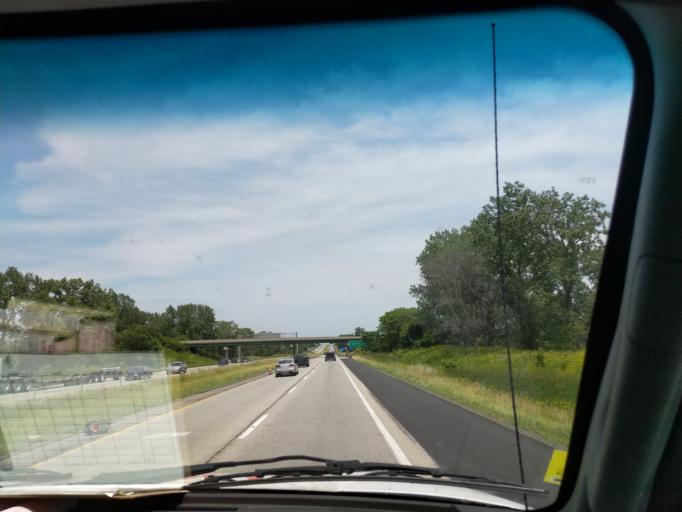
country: US
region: Iowa
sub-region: Dallas County
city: Waukee
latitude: 41.5789
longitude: -93.8344
